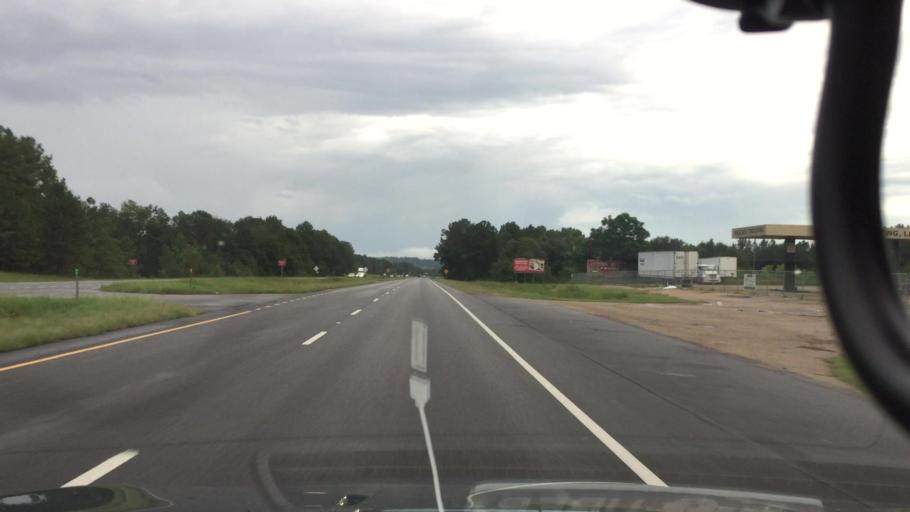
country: US
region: Alabama
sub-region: Pike County
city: Troy
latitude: 31.8830
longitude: -86.0059
